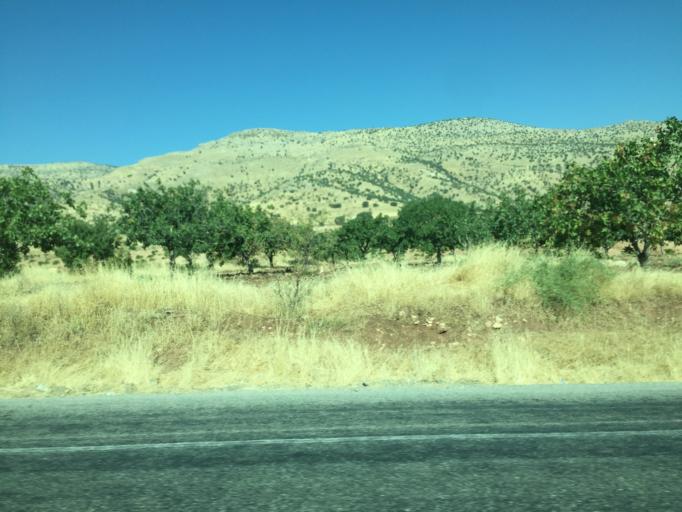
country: TR
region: Batman
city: Hasankeyf
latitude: 37.6704
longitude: 41.4549
